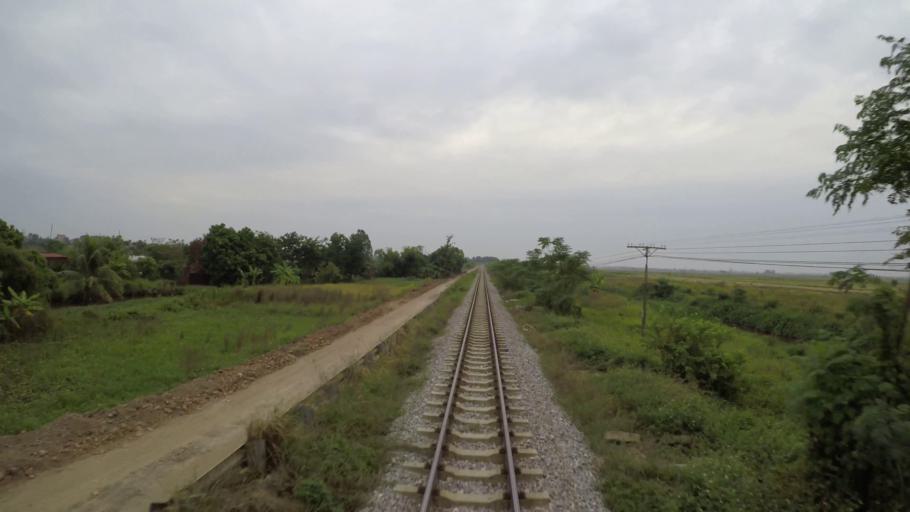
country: VN
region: Hai Duong
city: Ke Sat
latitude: 20.9657
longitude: 106.1269
